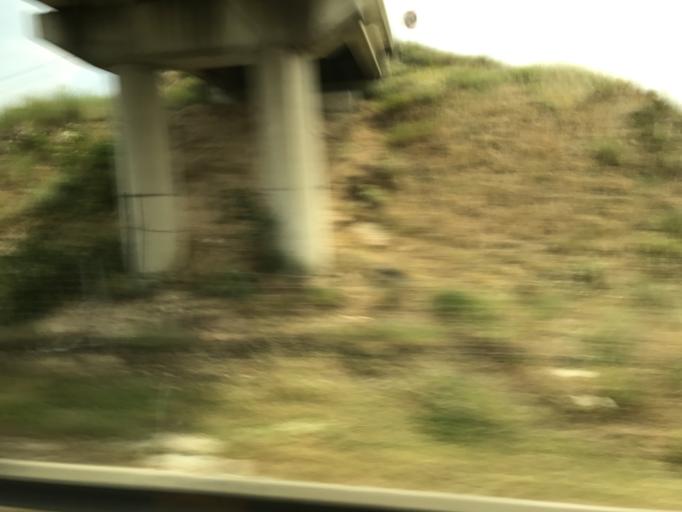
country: ES
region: Madrid
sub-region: Provincia de Madrid
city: Buitrago del Lozoya
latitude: 40.9489
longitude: -3.6393
